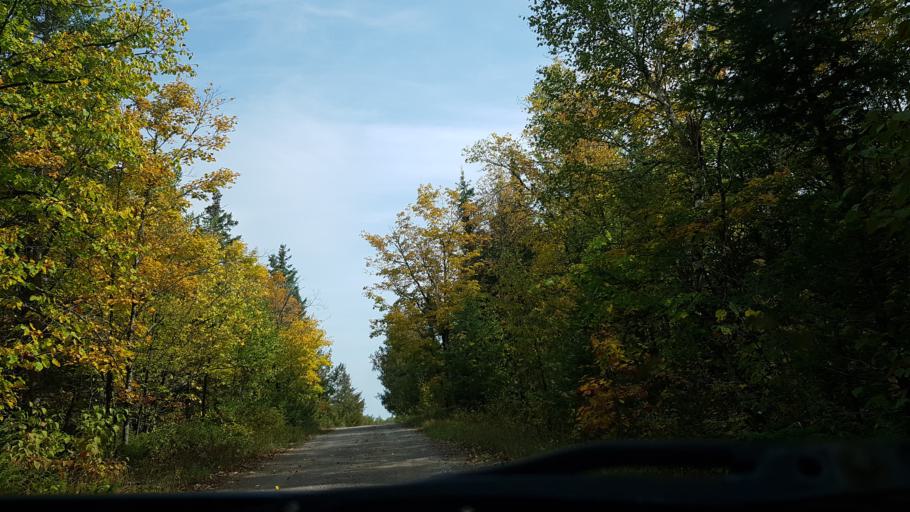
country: CA
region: Ontario
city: Orillia
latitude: 44.6833
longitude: -79.0584
